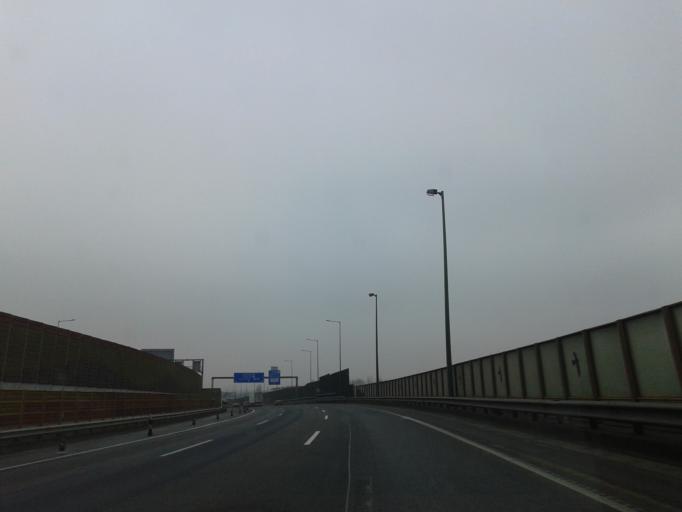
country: HU
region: Budapest
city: Budapest XXII. keruelet
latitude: 47.4009
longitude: 19.0051
